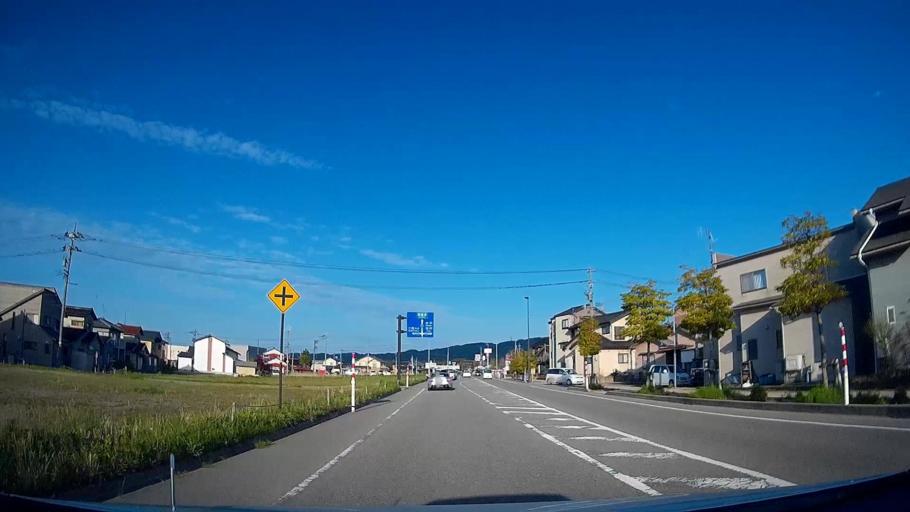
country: JP
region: Ishikawa
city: Nanao
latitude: 37.0320
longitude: 136.9651
